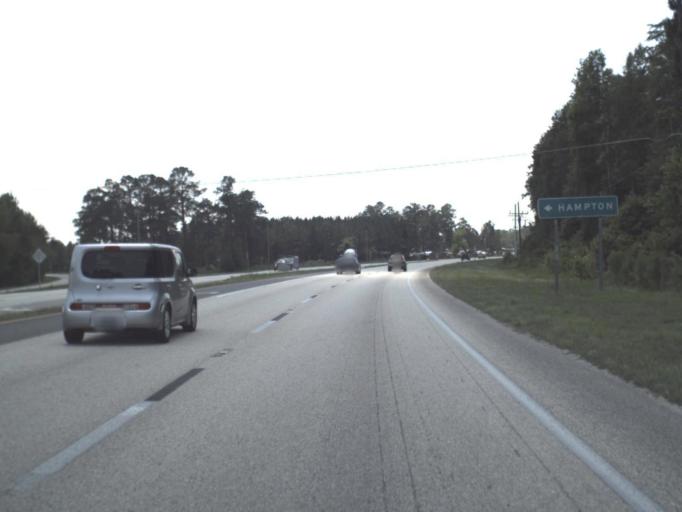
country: US
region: Florida
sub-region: Bradford County
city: Starke
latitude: 29.8927
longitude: -82.1393
